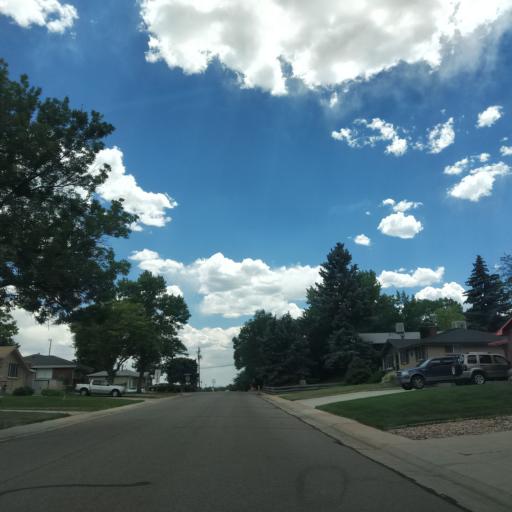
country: US
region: Colorado
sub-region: Jefferson County
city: Lakewood
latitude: 39.6868
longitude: -105.0862
